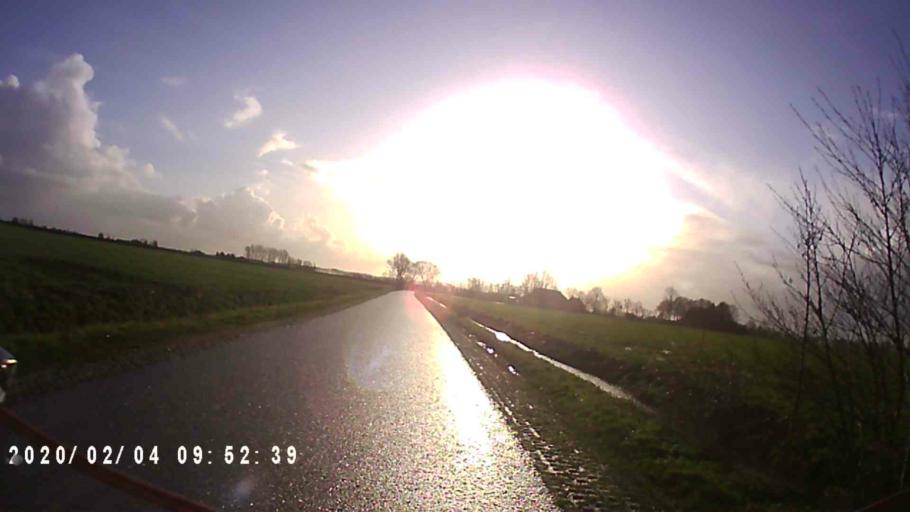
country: NL
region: Groningen
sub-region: Gemeente Zuidhorn
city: Aduard
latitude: 53.2839
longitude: 6.4961
